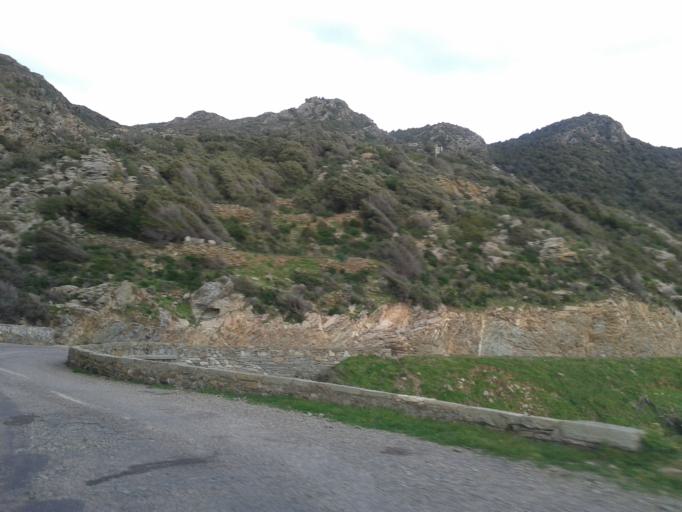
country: FR
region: Corsica
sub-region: Departement de la Haute-Corse
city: Brando
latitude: 42.8912
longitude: 9.3318
